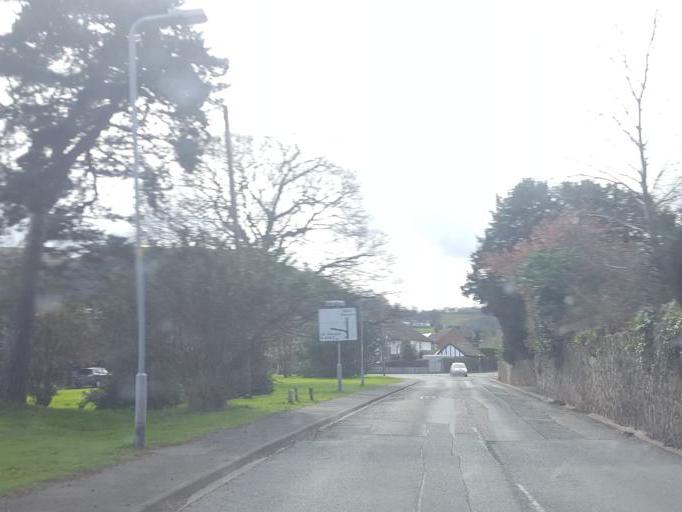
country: GB
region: England
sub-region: Worcestershire
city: Great Malvern
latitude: 52.1312
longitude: -2.3311
